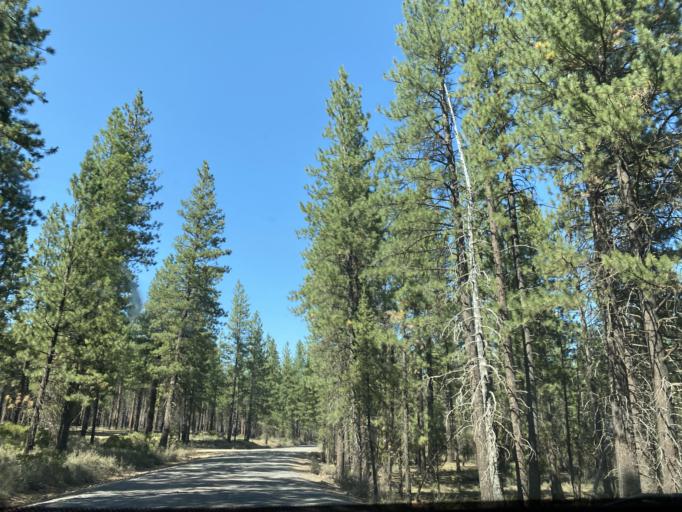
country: US
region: Oregon
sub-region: Deschutes County
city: Three Rivers
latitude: 43.8648
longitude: -121.4862
